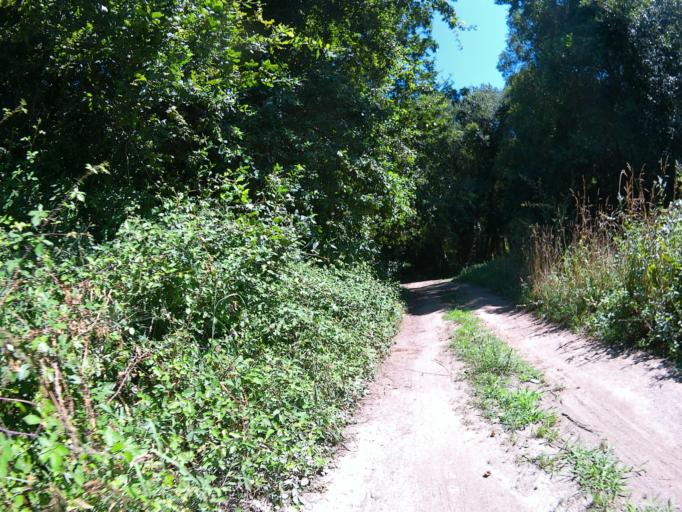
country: PT
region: Viana do Castelo
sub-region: Viana do Castelo
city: Darque
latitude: 41.7112
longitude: -8.7099
